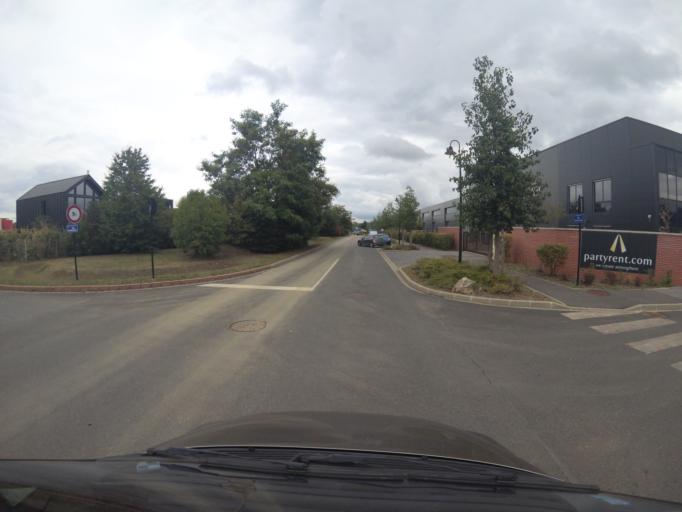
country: FR
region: Ile-de-France
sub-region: Departement de Seine-et-Marne
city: Chessy
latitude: 48.8789
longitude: 2.7757
